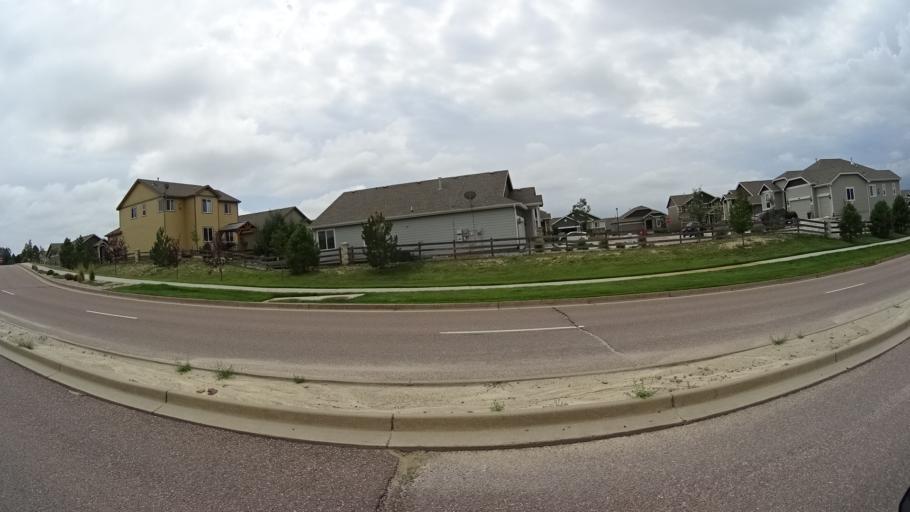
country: US
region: Colorado
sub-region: El Paso County
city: Gleneagle
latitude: 39.0130
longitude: -104.8108
